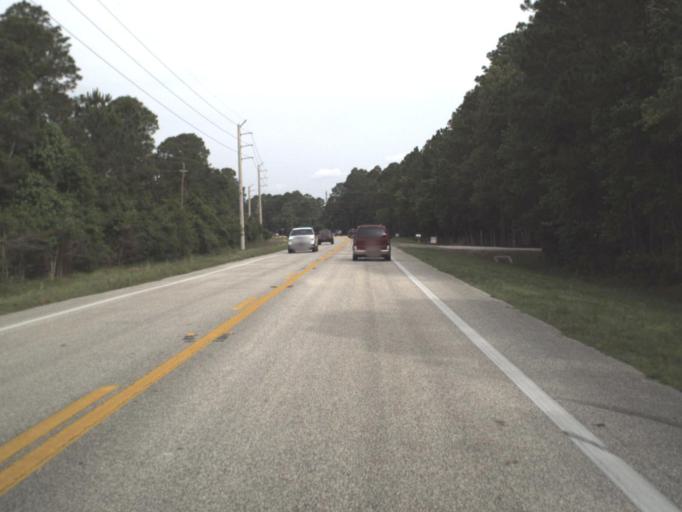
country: US
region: Florida
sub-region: Saint Johns County
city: Saint Augustine
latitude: 29.9553
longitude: -81.4590
